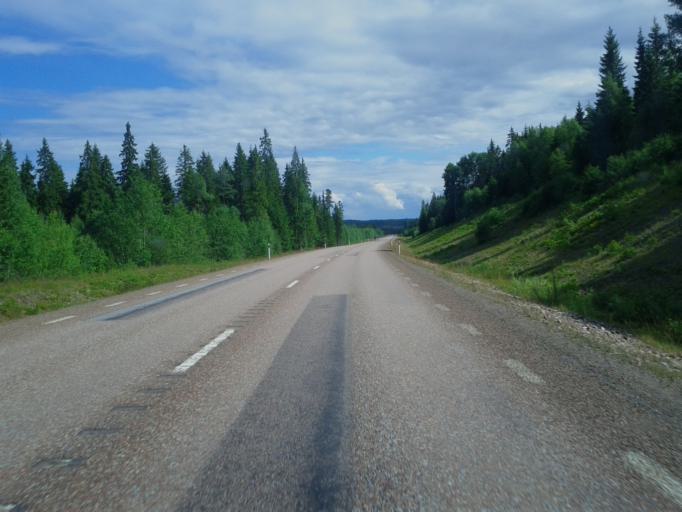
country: SE
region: Dalarna
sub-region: Rattviks Kommun
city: Raettvik
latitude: 60.8323
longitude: 15.2370
